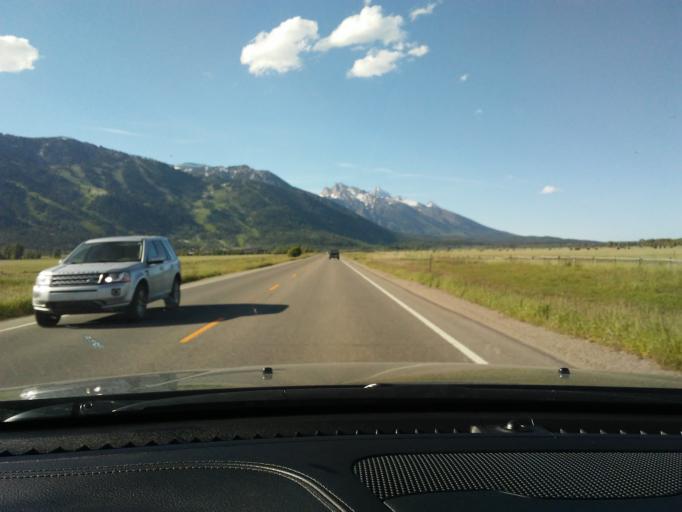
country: US
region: Wyoming
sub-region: Teton County
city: Moose Wilson Road
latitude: 43.5632
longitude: -110.8220
